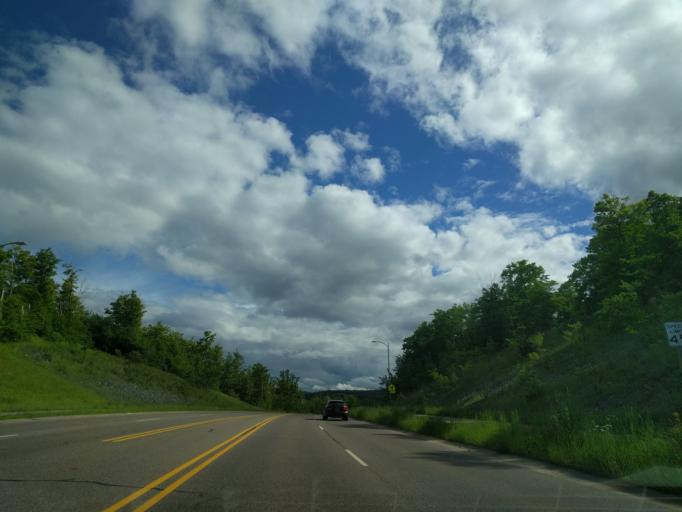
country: US
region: Michigan
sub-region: Marquette County
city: Marquette
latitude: 46.5361
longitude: -87.4172
